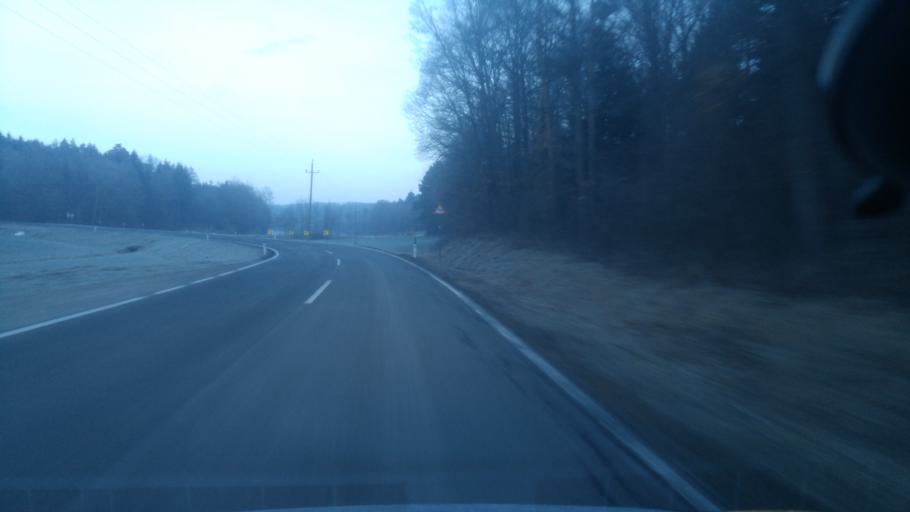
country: AT
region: Lower Austria
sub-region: Politischer Bezirk Baden
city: Berndorf
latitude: 47.9587
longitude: 16.1404
